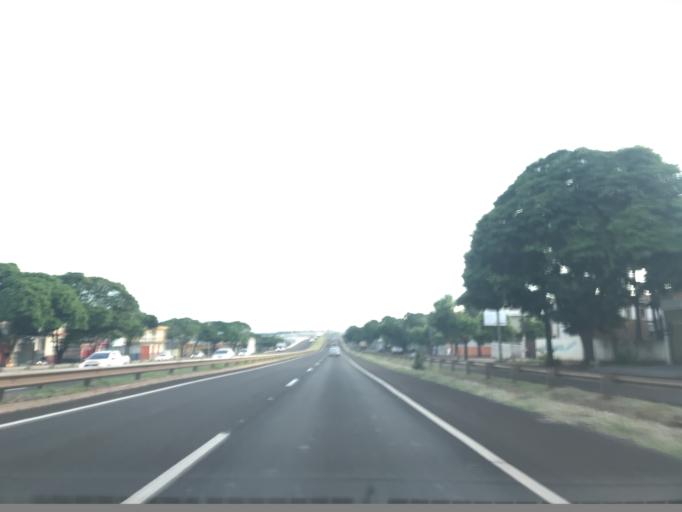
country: BR
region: Parana
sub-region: Maringa
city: Maringa
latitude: -23.3981
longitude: -51.9765
